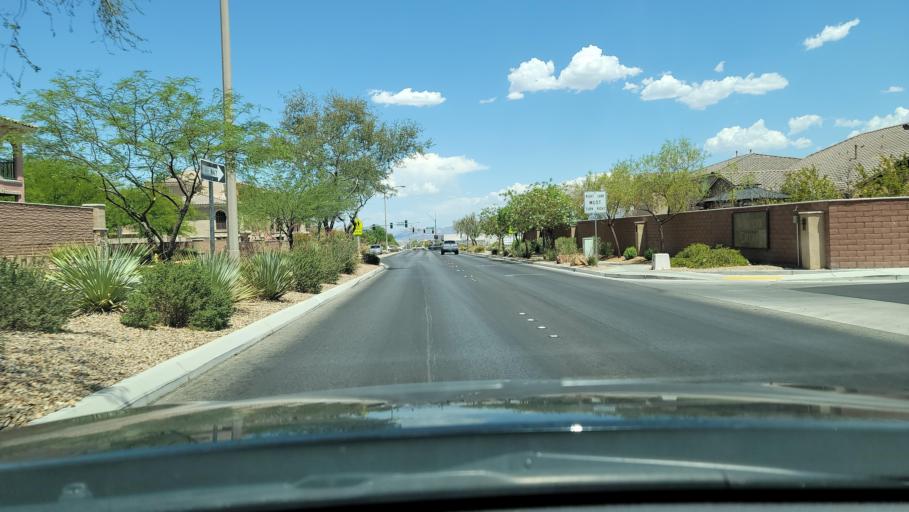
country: US
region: Nevada
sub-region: Clark County
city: Enterprise
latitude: 36.0052
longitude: -115.2639
